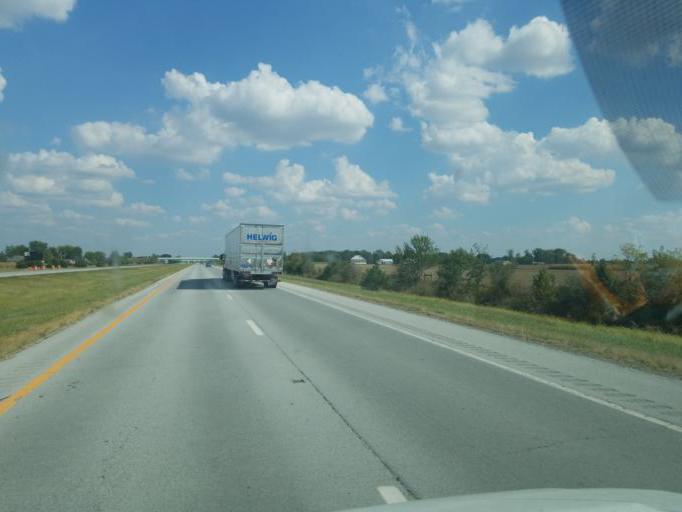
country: US
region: Ohio
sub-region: Allen County
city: Delphos
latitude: 40.8733
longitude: -84.3868
